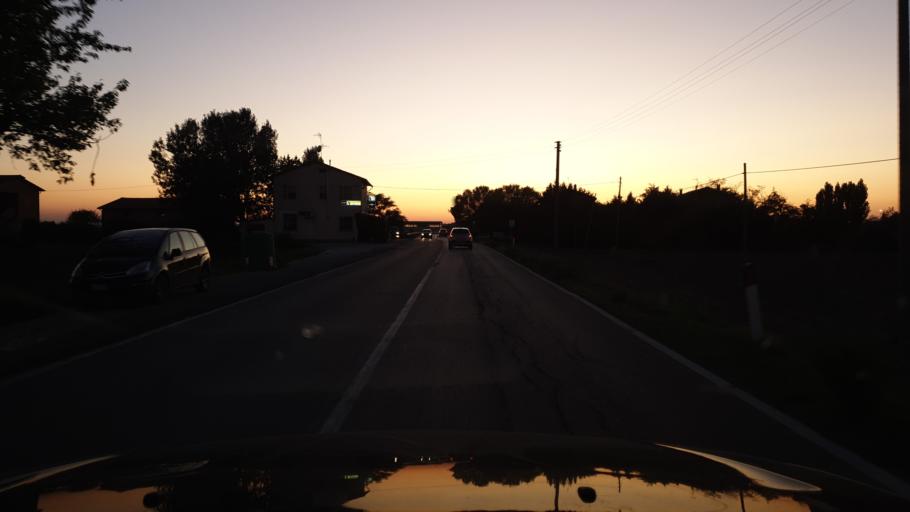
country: IT
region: Emilia-Romagna
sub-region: Provincia di Bologna
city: Altedo
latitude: 44.6842
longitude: 11.4870
